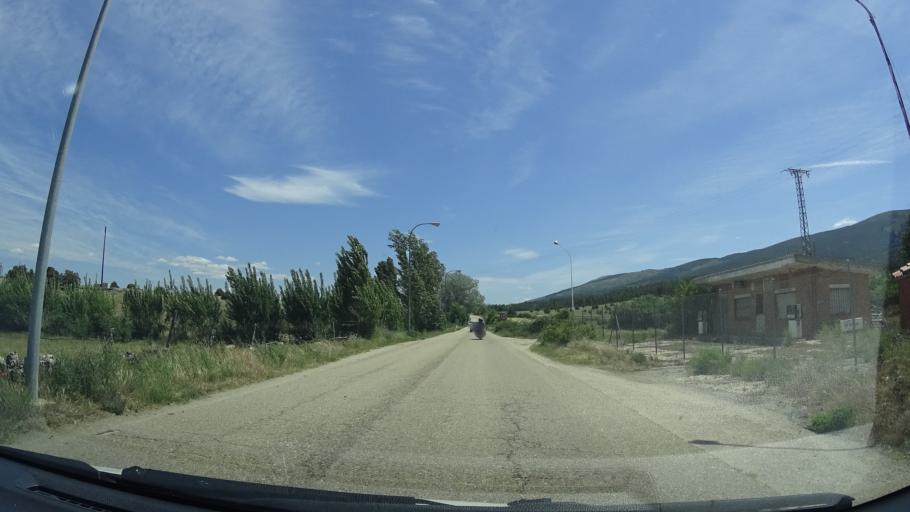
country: ES
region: Castille and Leon
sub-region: Provincia de Segovia
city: Pradena
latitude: 41.1418
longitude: -3.6811
